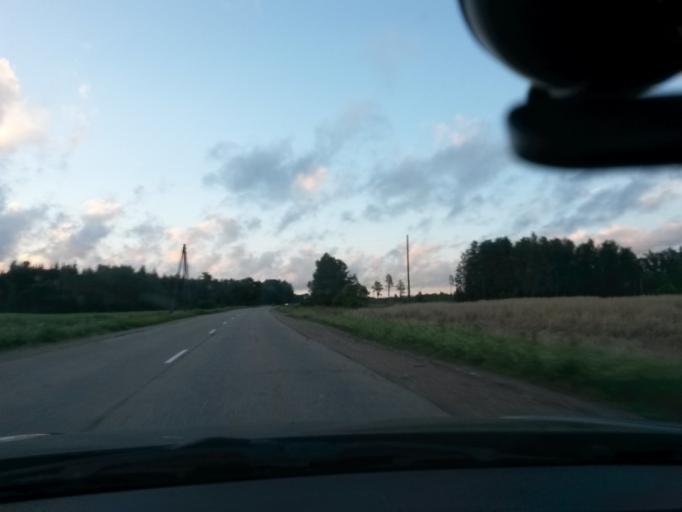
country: LV
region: Jekabpils Rajons
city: Jekabpils
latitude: 56.7027
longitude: 25.9812
